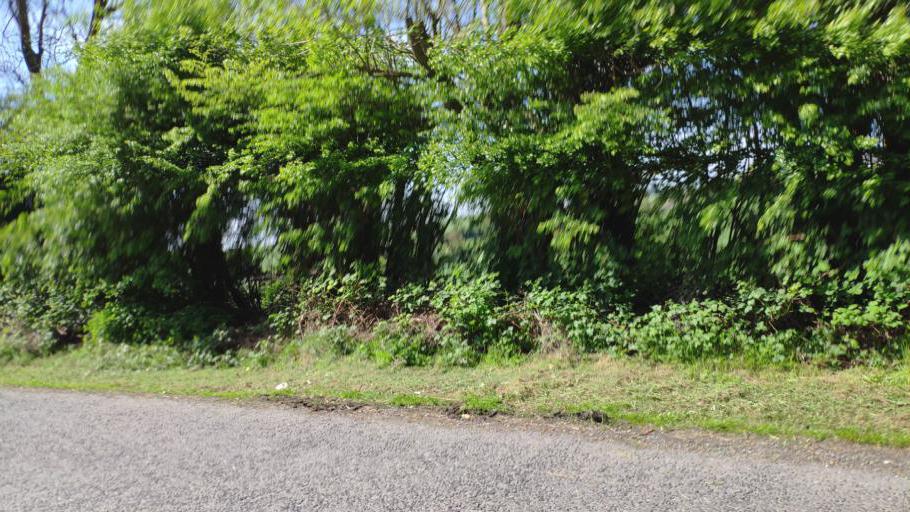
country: IE
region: Munster
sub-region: County Cork
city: Blarney
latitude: 51.9573
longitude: -8.5754
